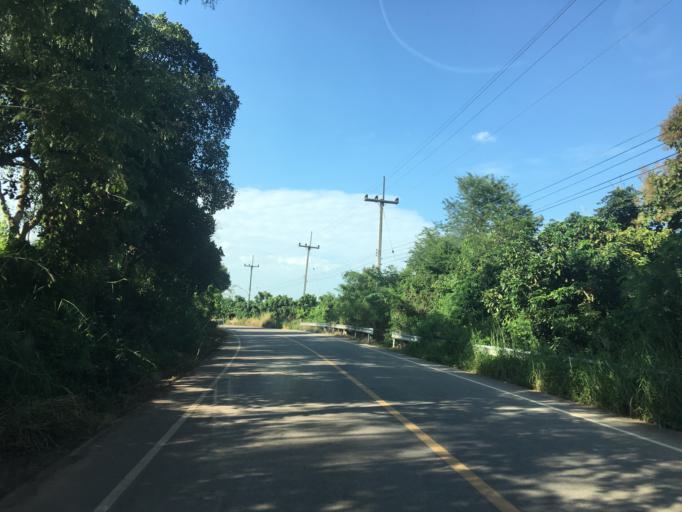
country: TH
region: Chiang Rai
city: Pa Daet
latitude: 19.4291
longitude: 100.0146
